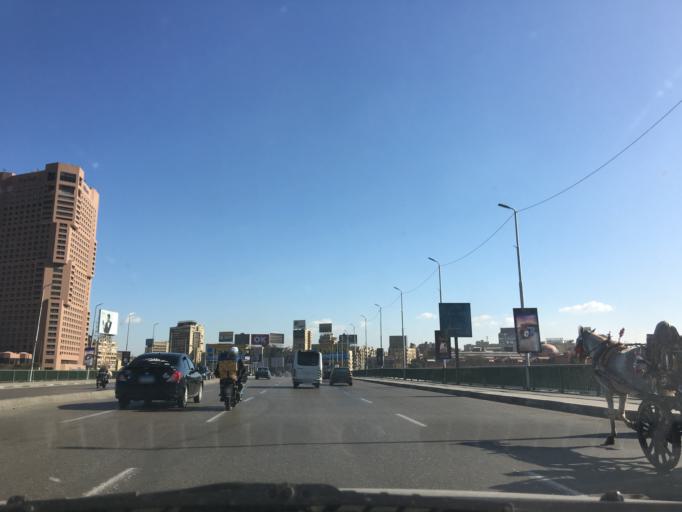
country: EG
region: Muhafazat al Qahirah
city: Cairo
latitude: 30.0491
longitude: 31.2287
